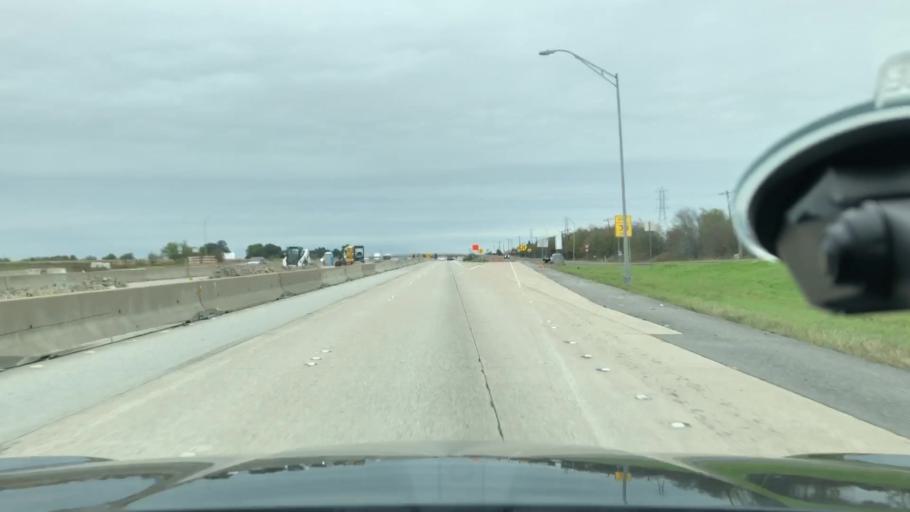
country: US
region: Texas
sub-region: Ellis County
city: Waxahachie
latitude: 32.3522
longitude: -96.8546
